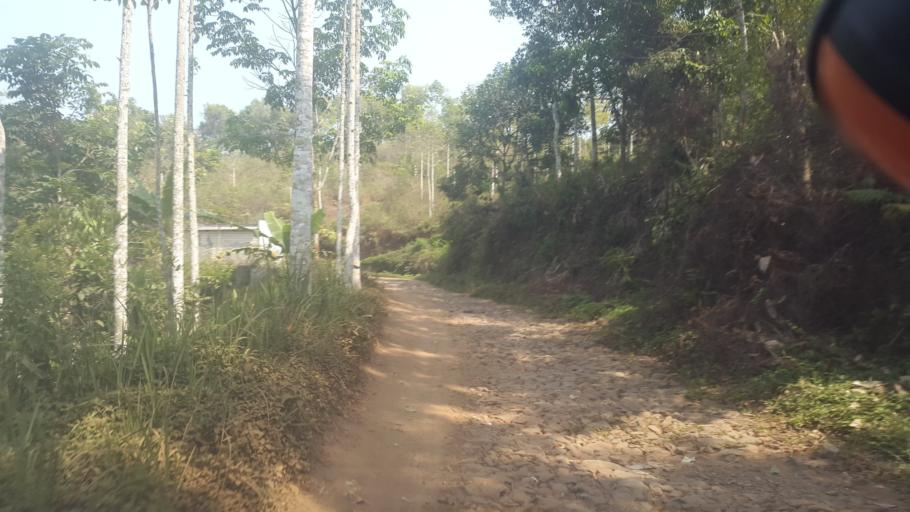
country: ID
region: West Java
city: Cijapar
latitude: -6.8923
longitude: 106.4323
